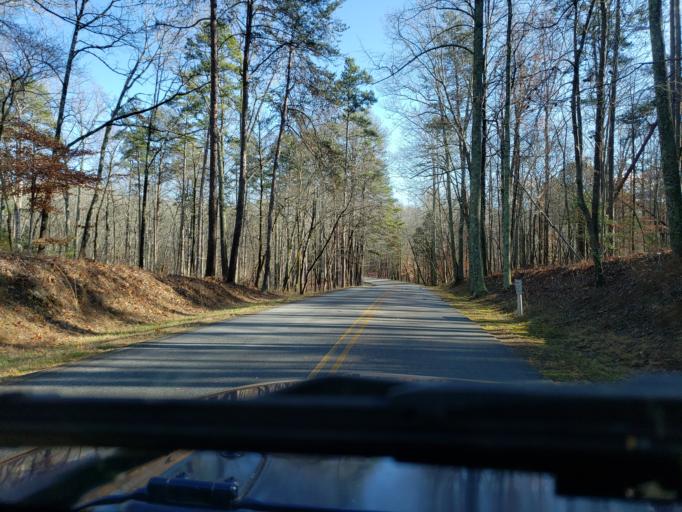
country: US
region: North Carolina
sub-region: Cleveland County
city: White Plains
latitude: 35.1513
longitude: -81.3934
